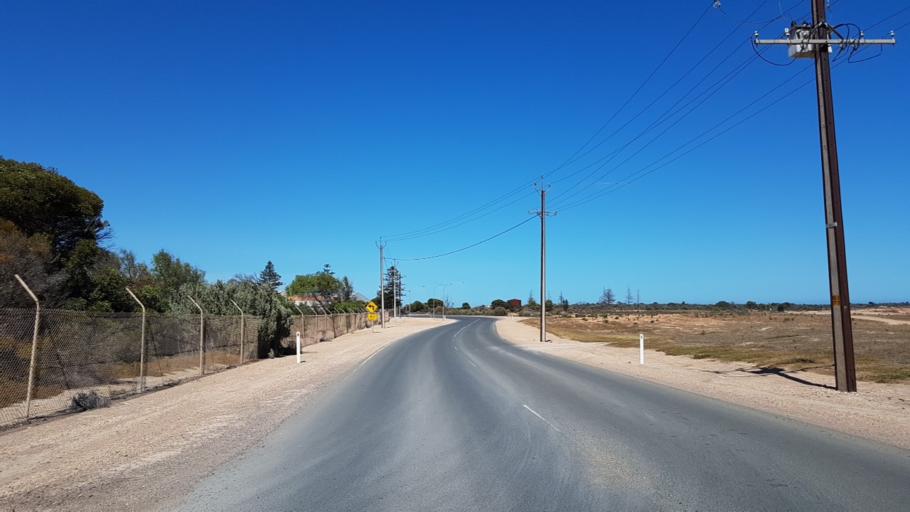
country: AU
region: South Australia
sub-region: Copper Coast
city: Wallaroo
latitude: -33.9350
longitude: 137.6093
